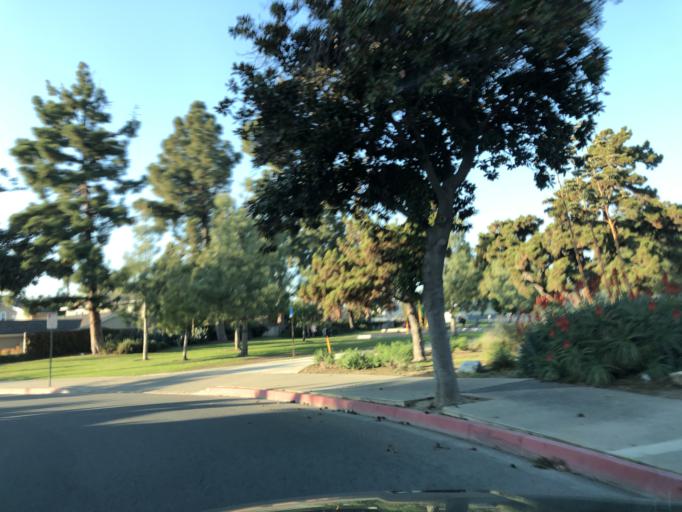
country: US
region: California
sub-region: Orange County
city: Orange
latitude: 33.7646
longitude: -117.8441
